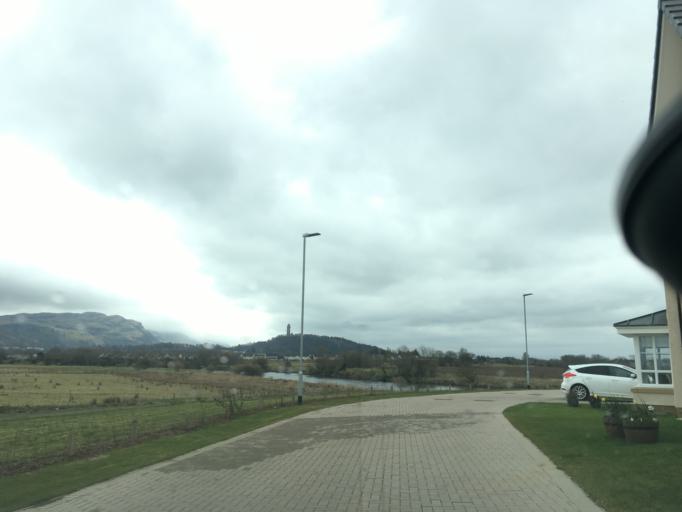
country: GB
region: Scotland
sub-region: Stirling
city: Bridge of Allan
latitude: 56.1358
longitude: -3.9600
